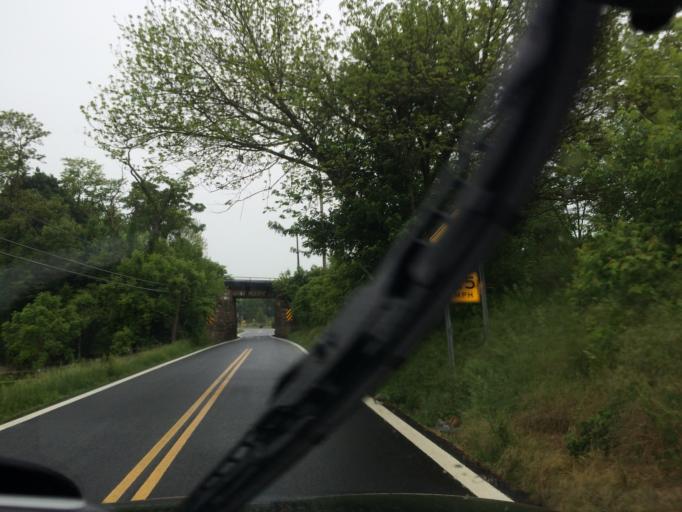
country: US
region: Maryland
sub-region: Frederick County
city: Thurmont
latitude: 39.6164
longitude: -77.3766
